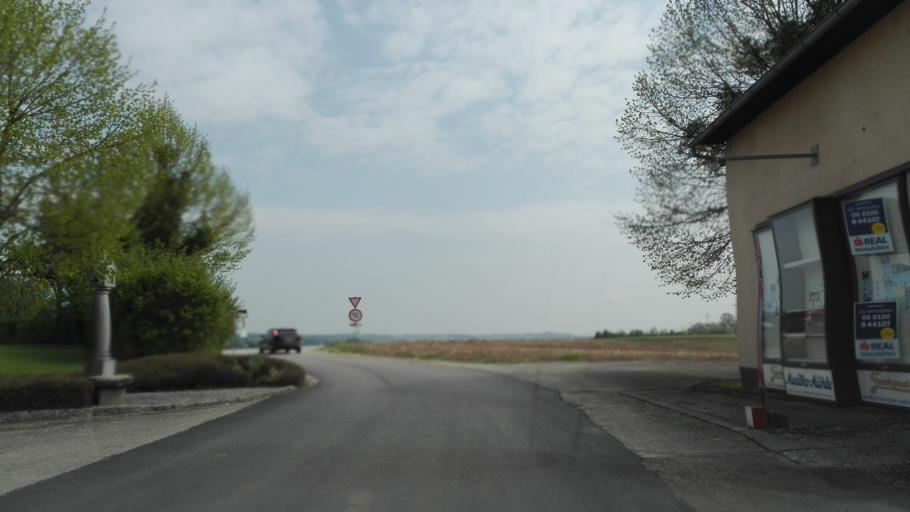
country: AT
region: Upper Austria
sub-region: Politischer Bezirk Perg
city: Perg
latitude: 48.2495
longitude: 14.5889
